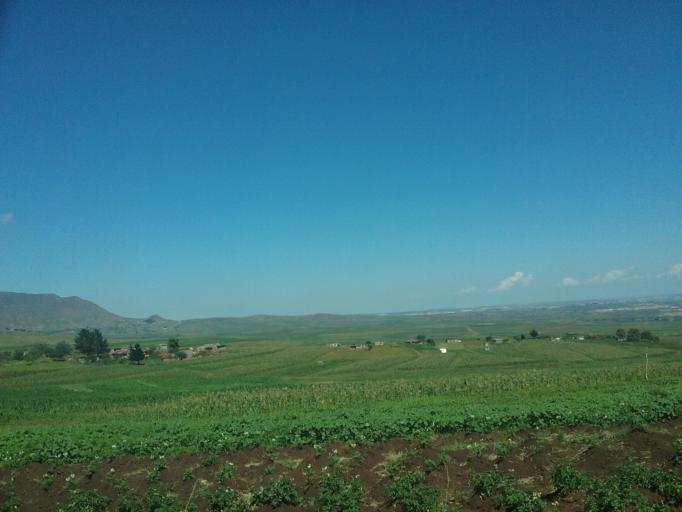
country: LS
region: Berea
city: Teyateyaneng
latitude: -29.2247
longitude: 27.8682
